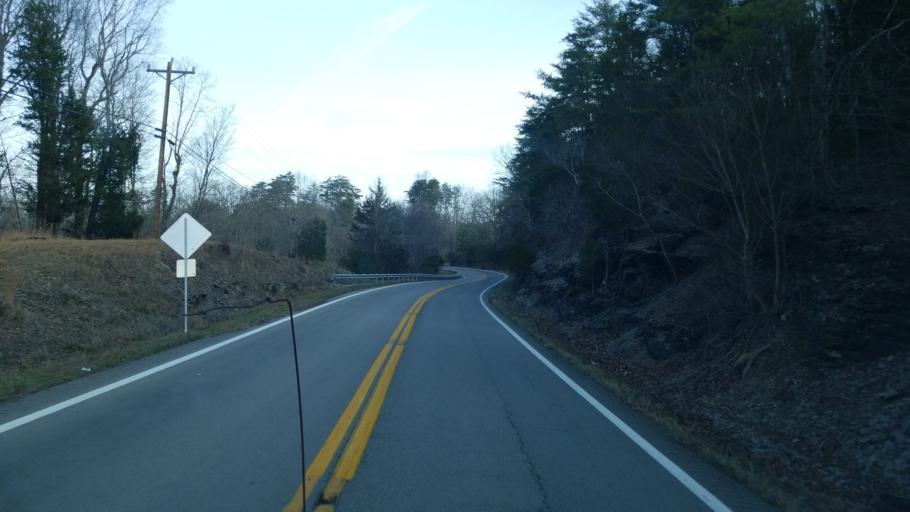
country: US
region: Kentucky
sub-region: Russell County
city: Jamestown
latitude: 36.8719
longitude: -85.1113
